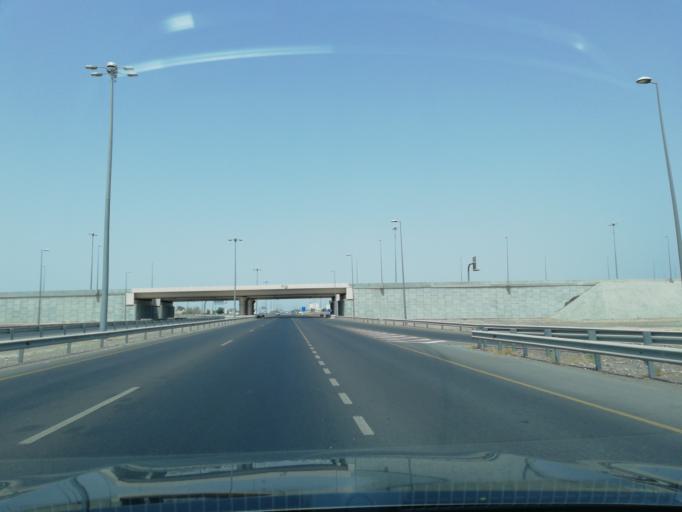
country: OM
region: Al Batinah
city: Barka'
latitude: 23.6862
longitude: 58.0260
